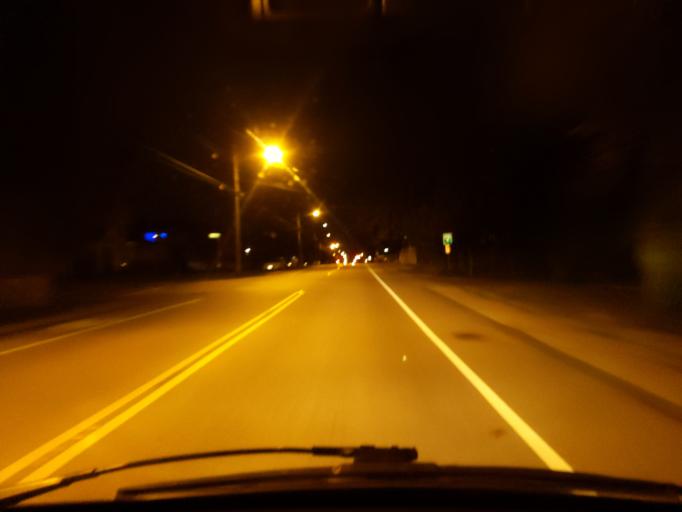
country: CA
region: British Columbia
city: New Westminster
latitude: 49.1956
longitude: -122.8677
